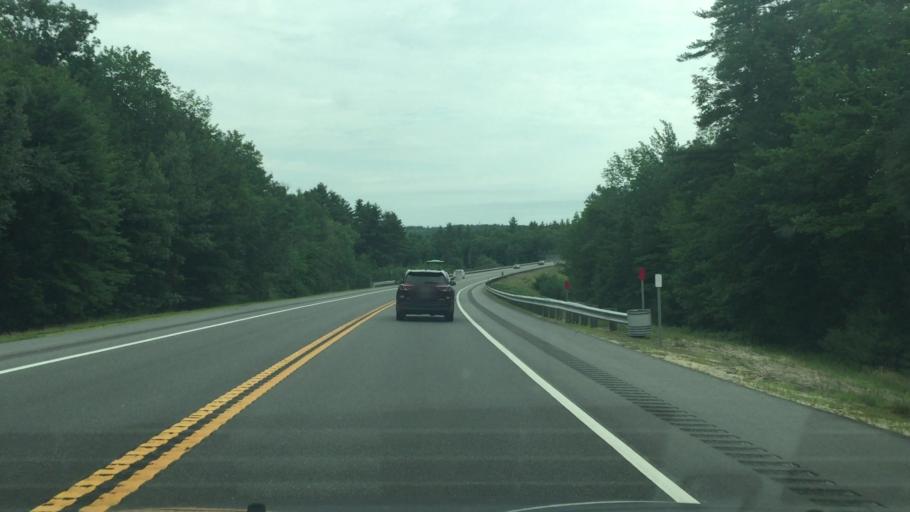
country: US
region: New Hampshire
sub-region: Strafford County
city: Farmington
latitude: 43.4546
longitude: -70.9940
